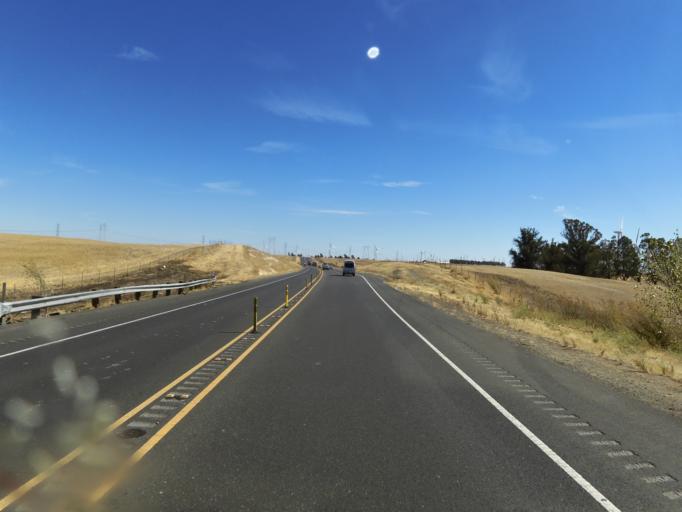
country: US
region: California
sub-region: Contra Costa County
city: Pittsburg
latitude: 38.1932
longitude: -121.8615
